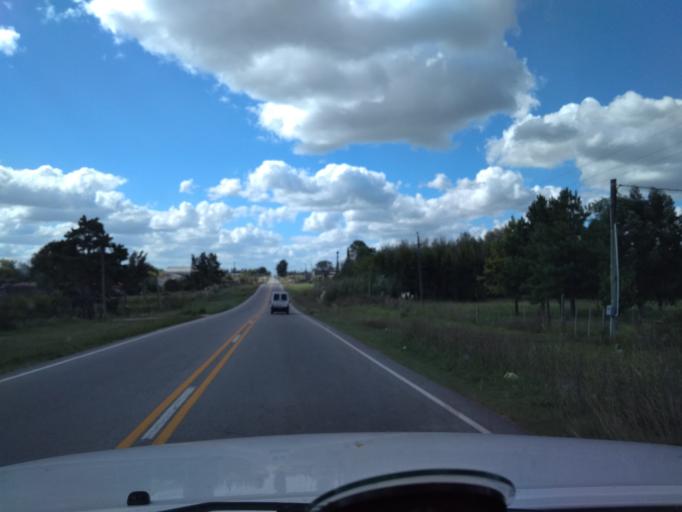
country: UY
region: Canelones
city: Joaquin Suarez
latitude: -34.6943
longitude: -56.0555
